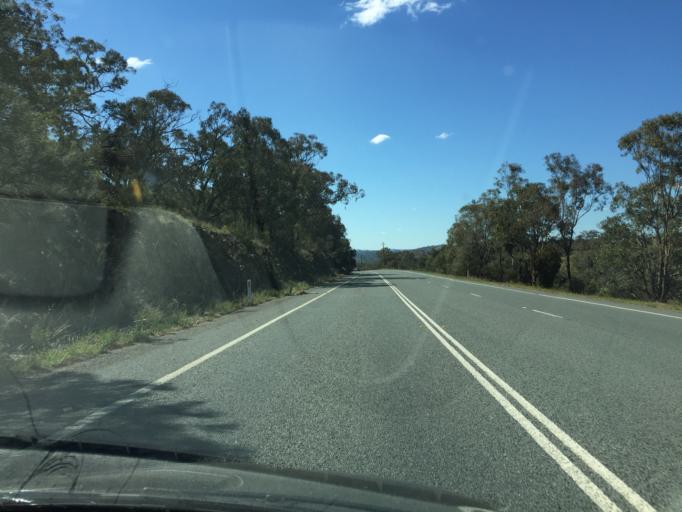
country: AU
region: Australian Capital Territory
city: Macarthur
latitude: -35.4609
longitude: 149.1333
